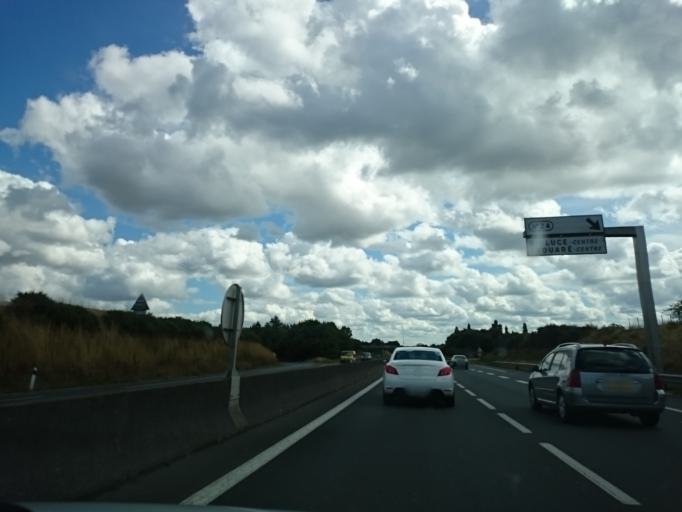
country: FR
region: Pays de la Loire
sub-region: Departement de la Loire-Atlantique
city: Sainte-Luce-sur-Loire
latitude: 47.2552
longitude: -1.4787
